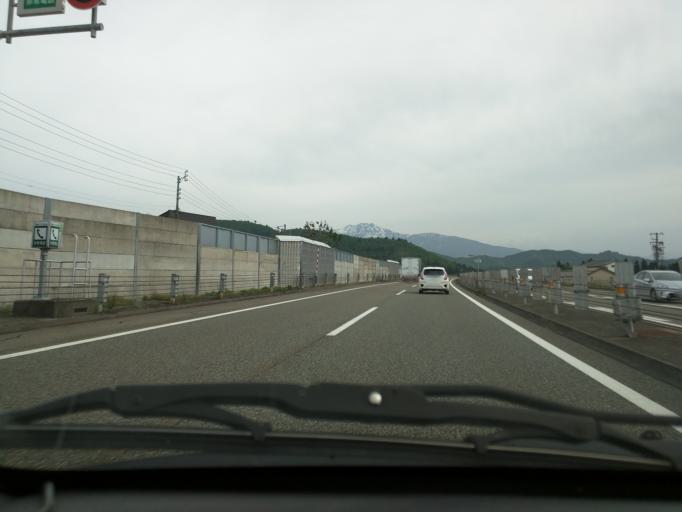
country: JP
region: Niigata
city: Muikamachi
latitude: 37.2288
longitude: 138.9773
